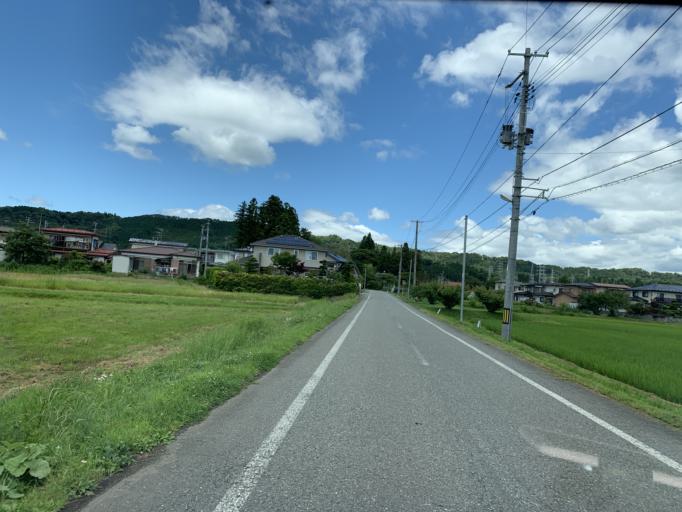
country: JP
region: Iwate
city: Ichinoseki
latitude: 38.9351
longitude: 141.0945
